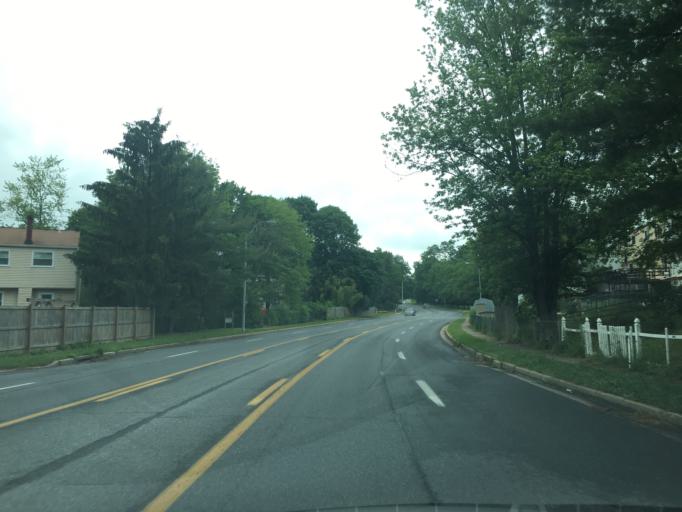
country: US
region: Maryland
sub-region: Baltimore County
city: Reisterstown
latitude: 39.4640
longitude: -76.8053
